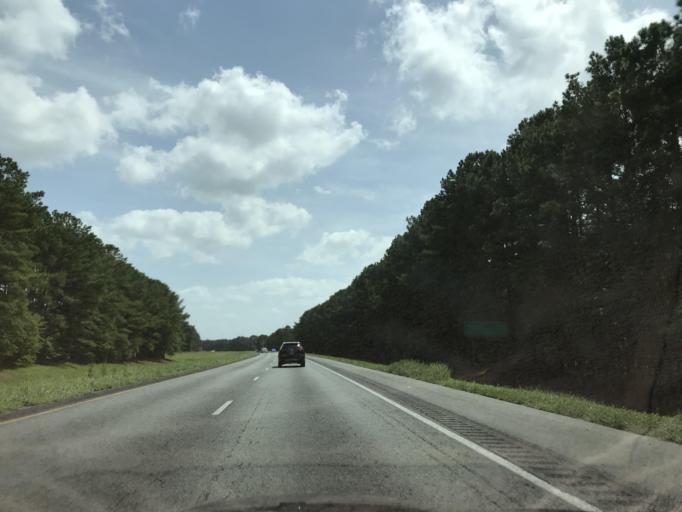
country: US
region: North Carolina
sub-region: Duplin County
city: Warsaw
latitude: 34.9818
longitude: -78.1304
